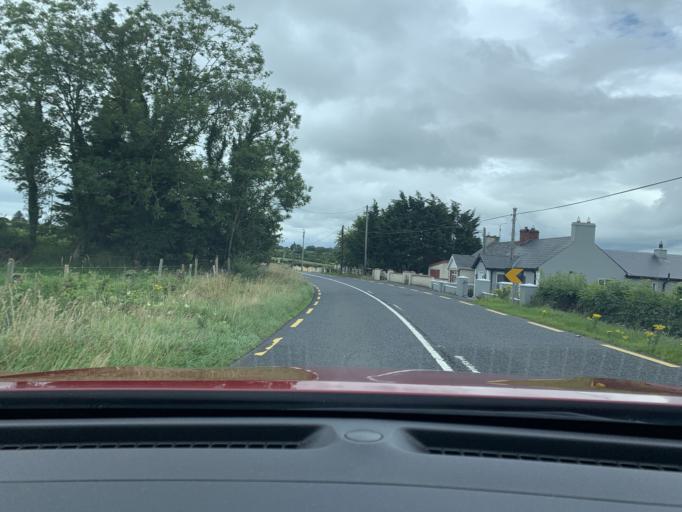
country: IE
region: Ulster
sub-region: County Donegal
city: Convoy
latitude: 54.7996
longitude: -7.6541
